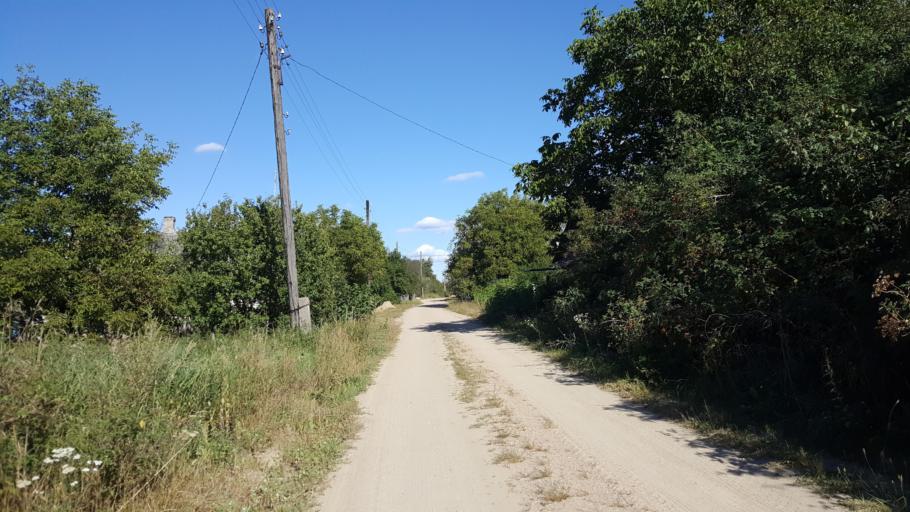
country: BY
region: Brest
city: Vysokaye
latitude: 52.3292
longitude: 23.5635
